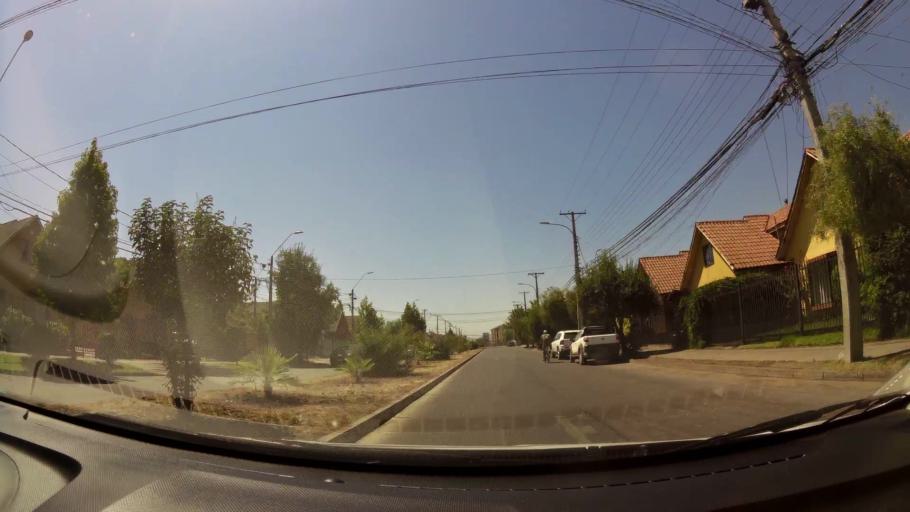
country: CL
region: Maule
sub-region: Provincia de Curico
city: Curico
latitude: -34.9715
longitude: -71.2224
